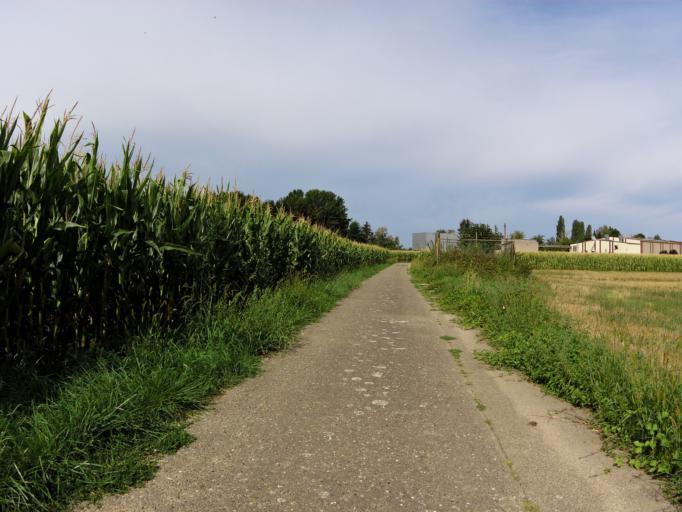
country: DE
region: Baden-Wuerttemberg
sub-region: Freiburg Region
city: Lahr
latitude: 48.3567
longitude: 7.8385
